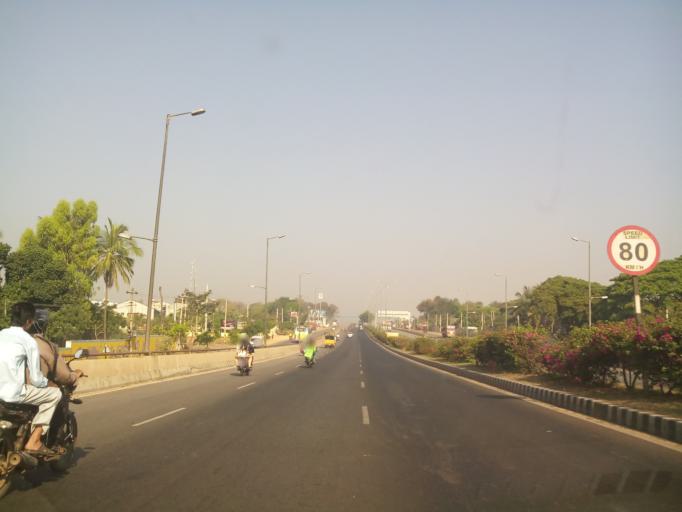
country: IN
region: Karnataka
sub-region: Bangalore Rural
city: Nelamangala
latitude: 13.0831
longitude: 77.4172
